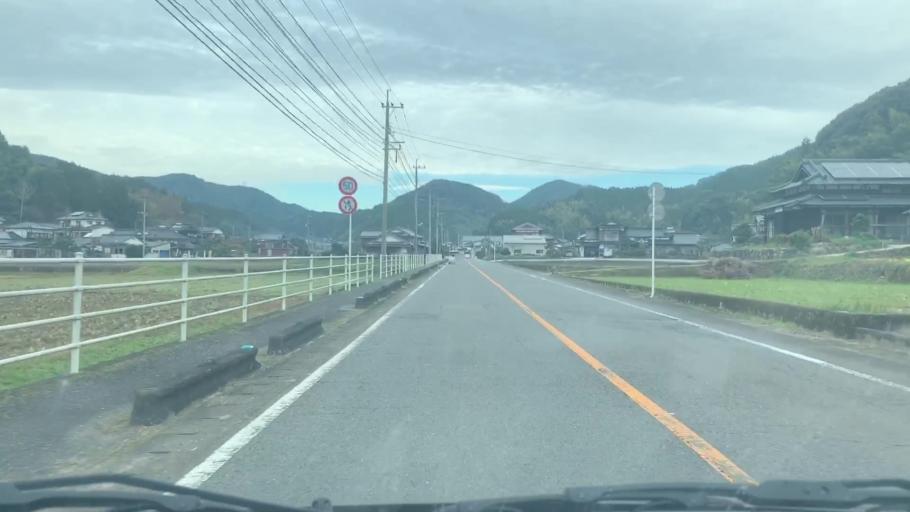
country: JP
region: Saga Prefecture
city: Ureshinomachi-shimojuku
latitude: 33.1435
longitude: 129.9765
